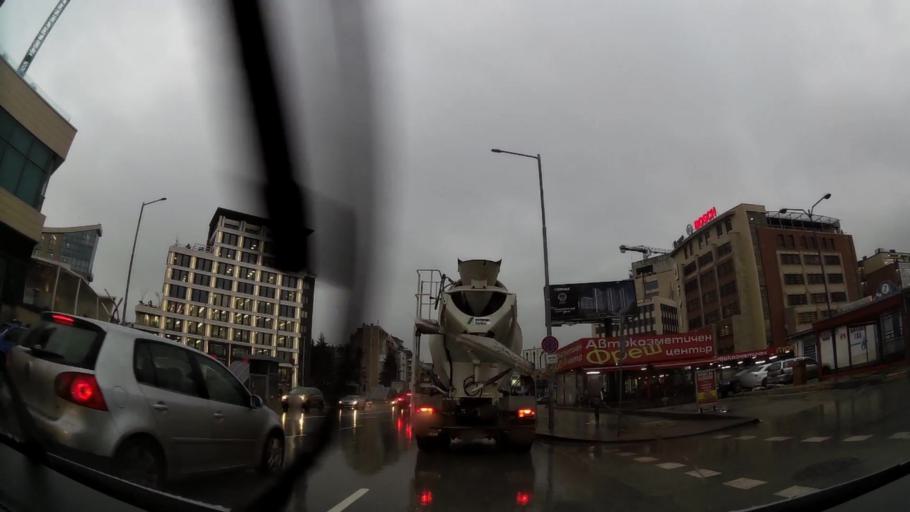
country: BG
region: Sofia-Capital
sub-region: Stolichna Obshtina
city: Sofia
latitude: 42.6585
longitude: 23.3164
